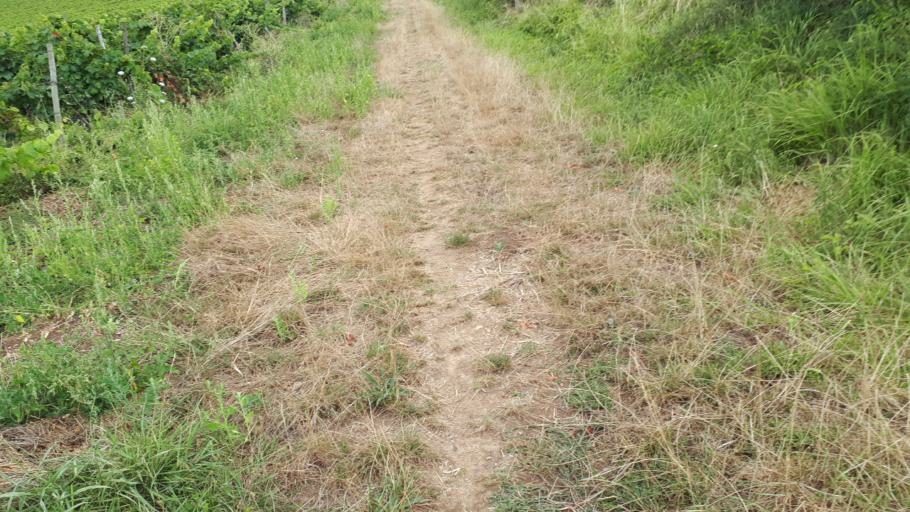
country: FR
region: Pays de la Loire
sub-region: Departement de Maine-et-Loire
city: Rochefort-sur-Loire
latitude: 47.3280
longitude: -0.6853
